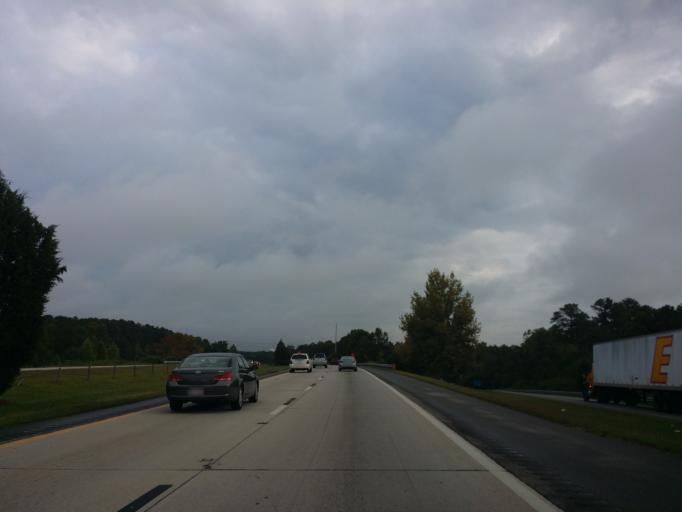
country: US
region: North Carolina
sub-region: Durham County
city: Durham
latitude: 35.9367
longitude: -78.8586
